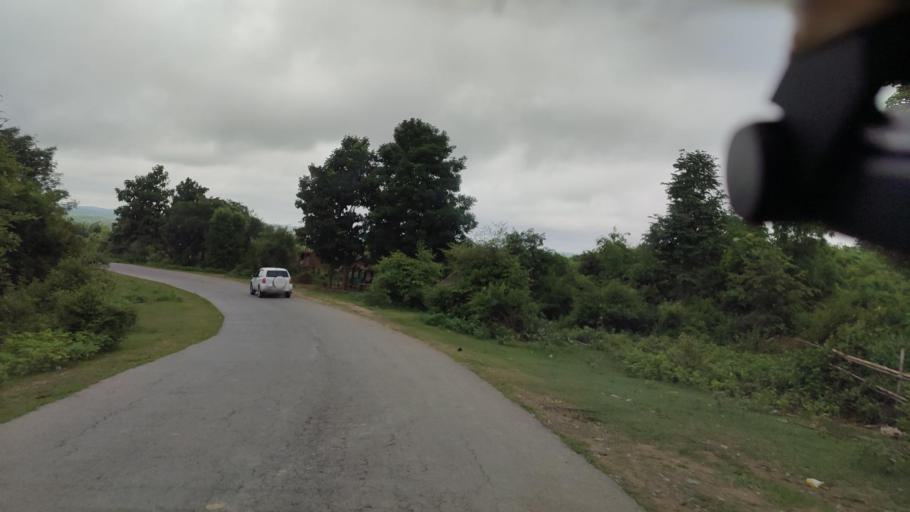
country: MM
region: Mandalay
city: Nay Pyi Taw
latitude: 19.9982
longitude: 95.9216
